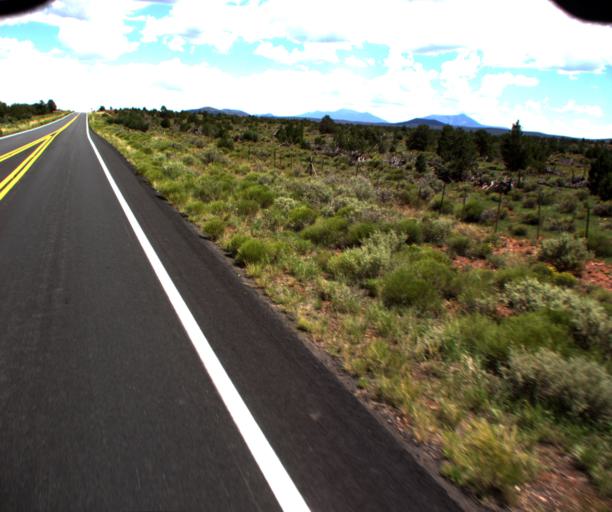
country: US
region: Arizona
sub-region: Coconino County
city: Parks
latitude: 35.6039
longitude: -112.0386
